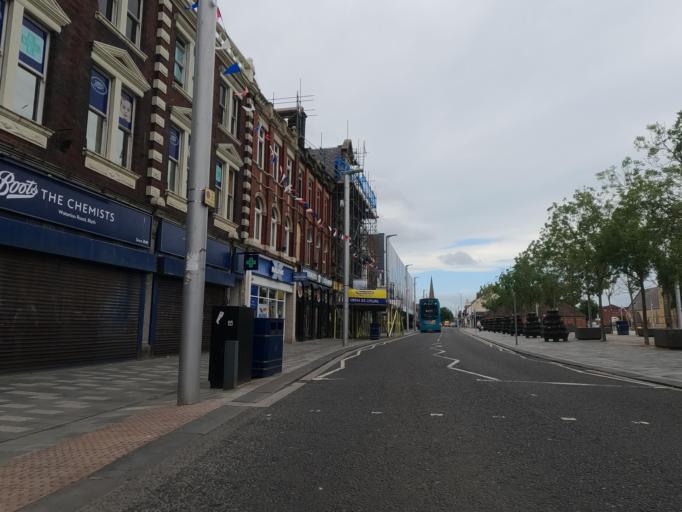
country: GB
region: England
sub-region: Northumberland
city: Blyth
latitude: 55.1270
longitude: -1.5094
